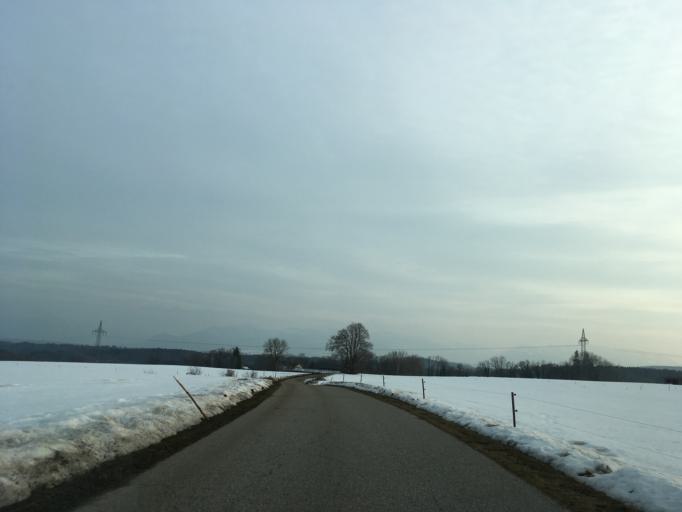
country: DE
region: Bavaria
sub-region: Upper Bavaria
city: Bad Endorf
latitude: 47.9161
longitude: 12.3317
